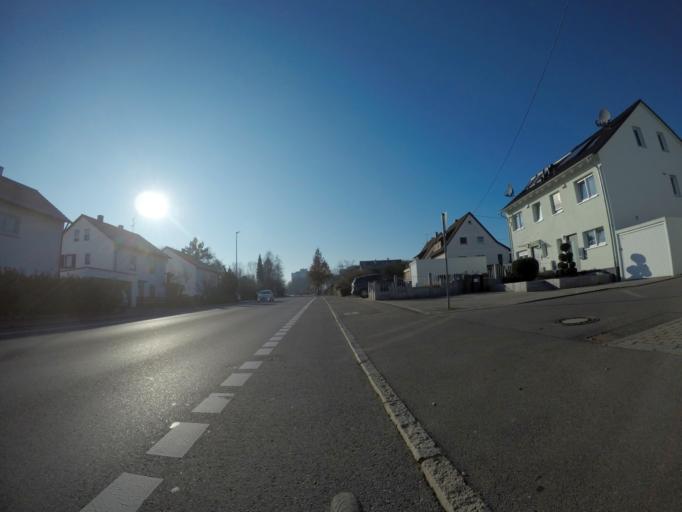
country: DE
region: Baden-Wuerttemberg
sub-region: Tuebingen Region
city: Reutlingen
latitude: 48.5138
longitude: 9.2229
